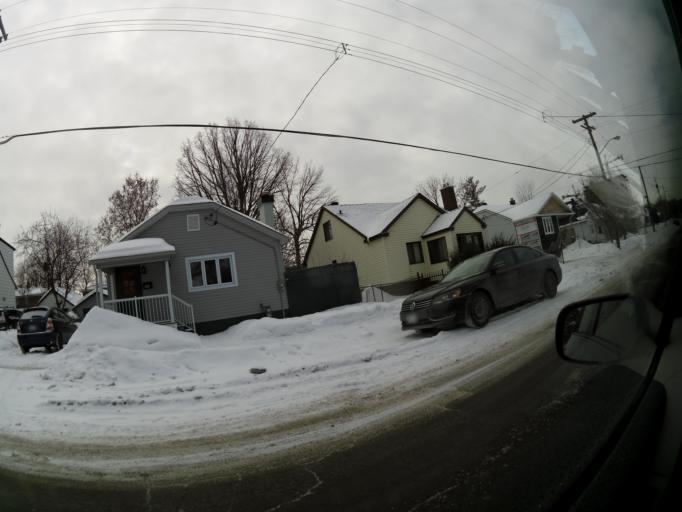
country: CA
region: Ontario
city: Ottawa
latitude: 45.4243
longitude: -75.6568
